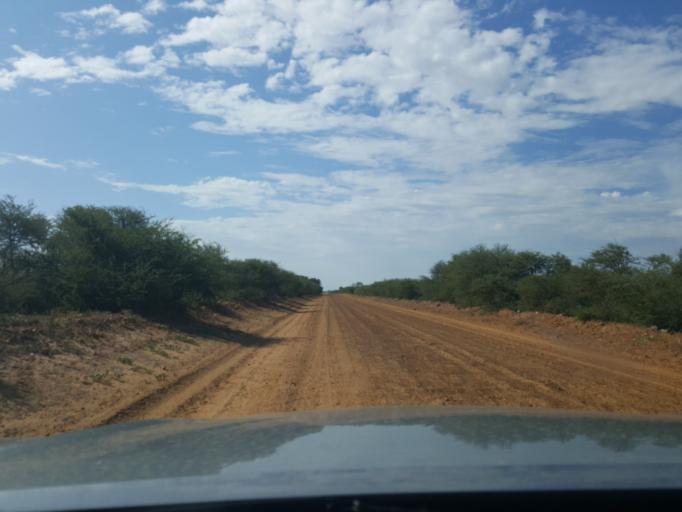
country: BW
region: Kweneng
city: Khudumelapye
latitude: -23.6277
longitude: 24.7279
